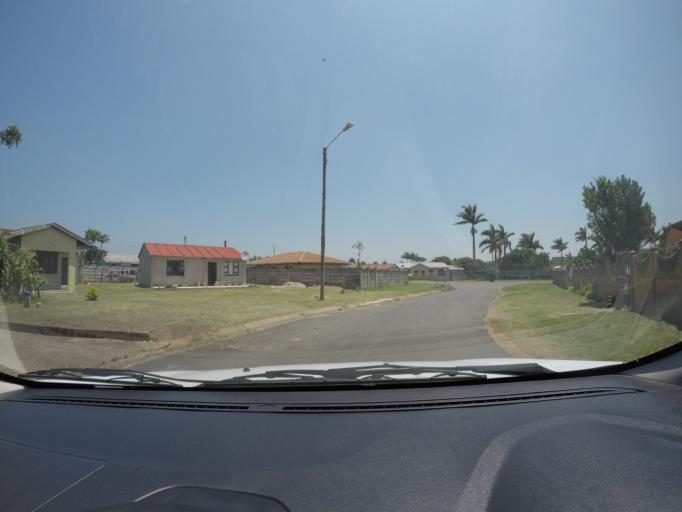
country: ZA
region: KwaZulu-Natal
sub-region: uThungulu District Municipality
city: eSikhawini
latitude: -28.8861
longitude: 31.8878
